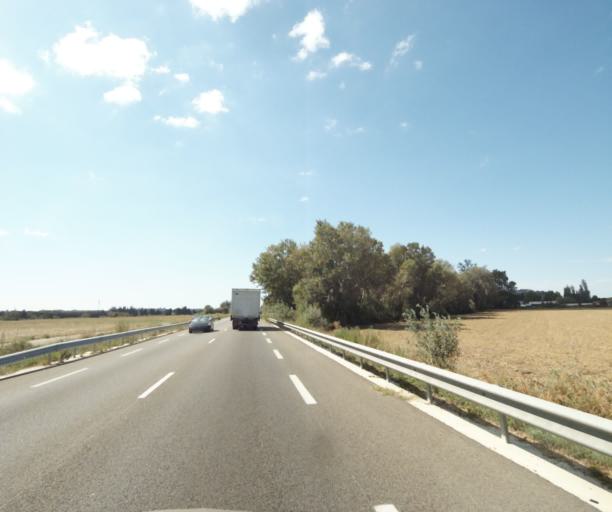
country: FR
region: Languedoc-Roussillon
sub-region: Departement du Gard
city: Rodilhan
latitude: 43.8190
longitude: 4.4164
